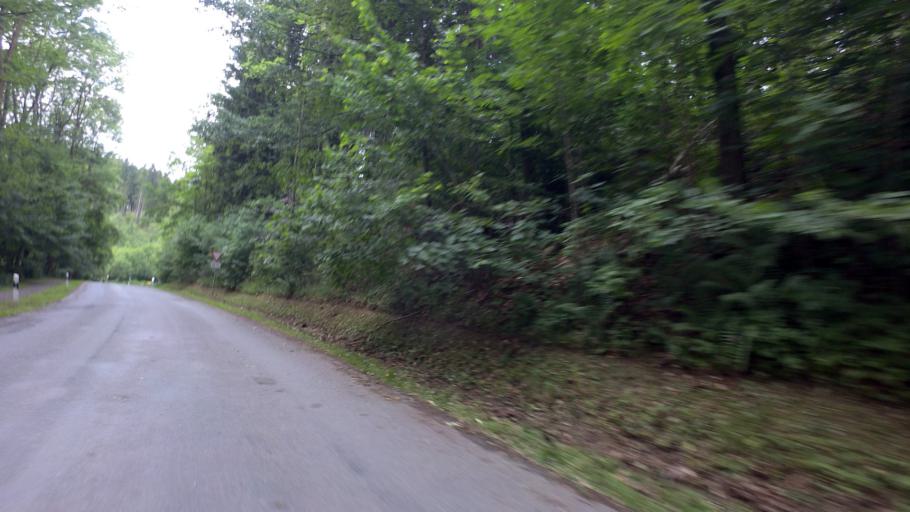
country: DE
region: Saxony
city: Sebnitz
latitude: 50.9790
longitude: 14.2627
